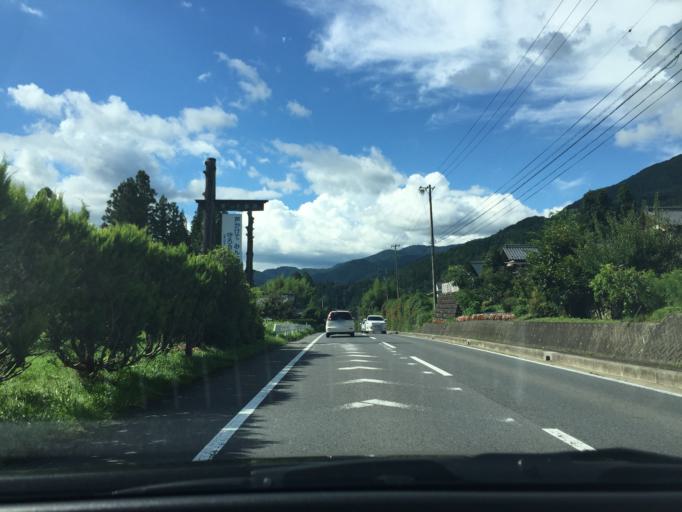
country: JP
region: Gifu
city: Nakatsugawa
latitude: 35.6568
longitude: 137.4332
